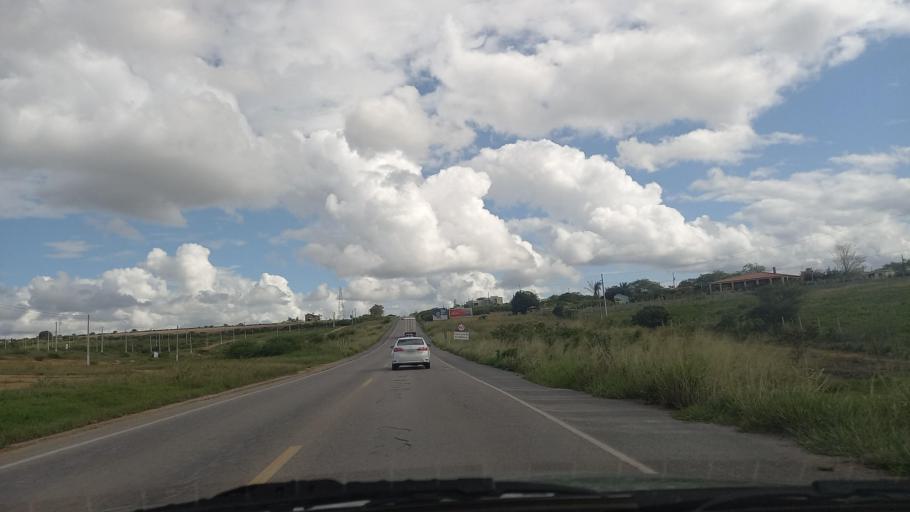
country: BR
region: Pernambuco
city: Garanhuns
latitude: -8.8269
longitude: -36.4512
